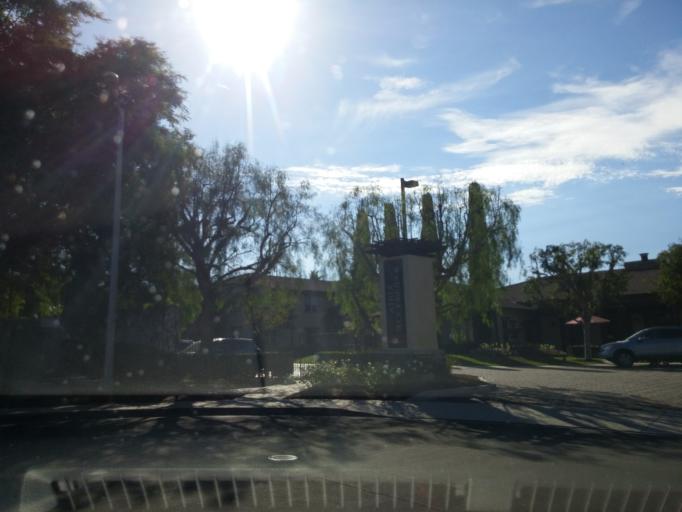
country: US
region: California
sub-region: Orange County
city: Irvine
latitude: 33.6728
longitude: -117.7922
